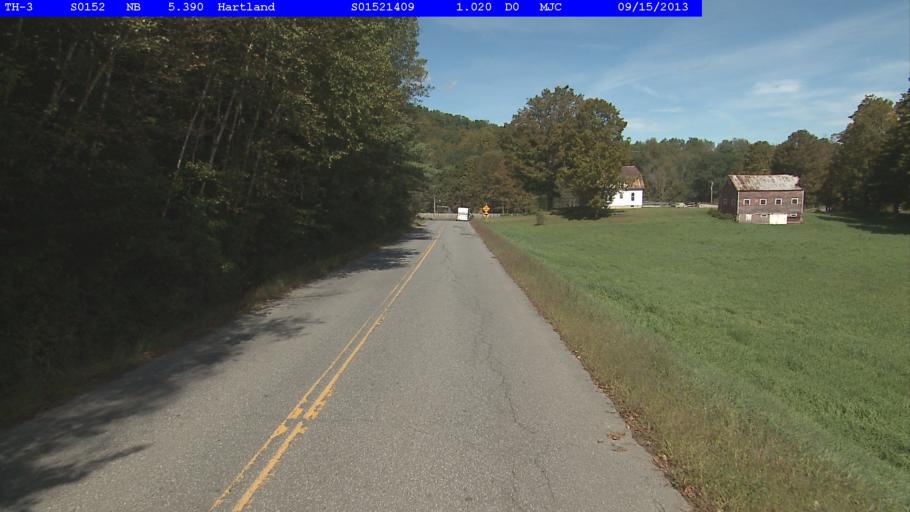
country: US
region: Vermont
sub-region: Windsor County
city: Windsor
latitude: 43.5357
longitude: -72.4337
